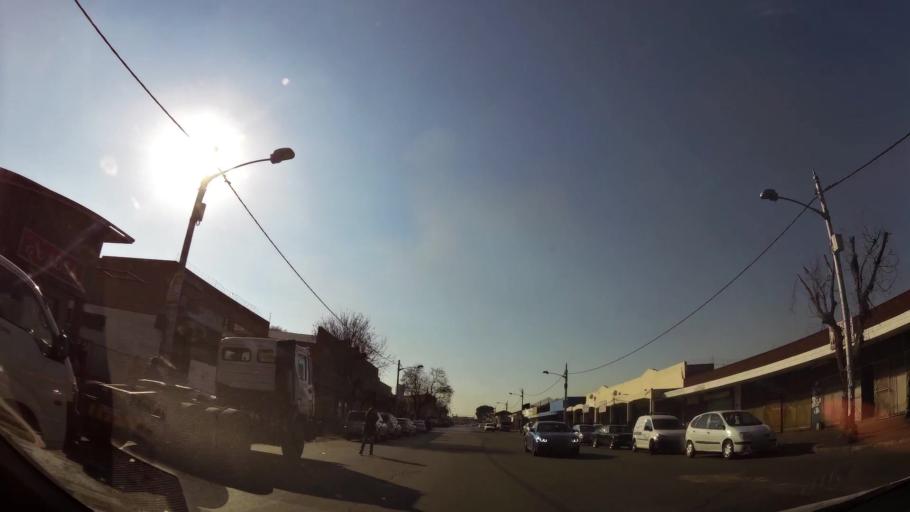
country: ZA
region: Gauteng
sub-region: Ekurhuleni Metropolitan Municipality
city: Germiston
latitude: -26.2013
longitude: 28.1161
